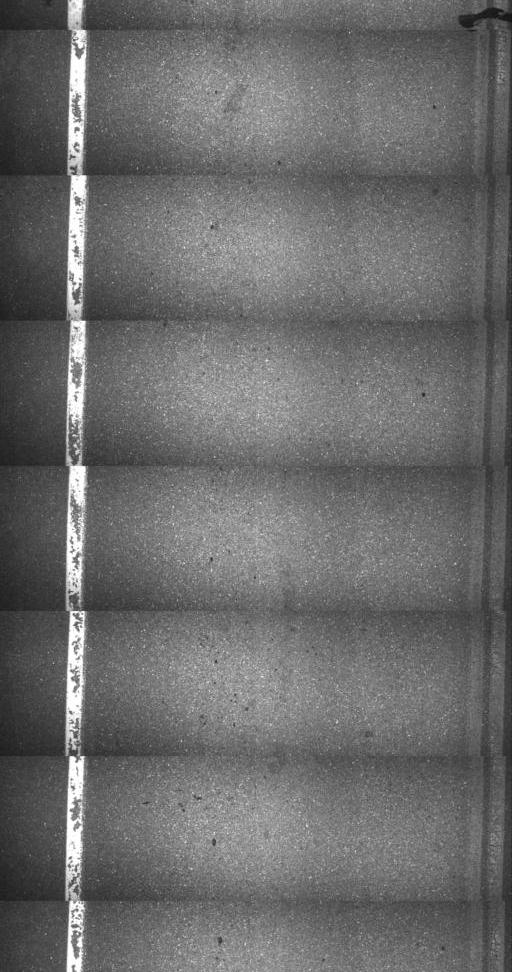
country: US
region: Vermont
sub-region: Orleans County
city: Newport
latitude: 44.9919
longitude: -72.3788
